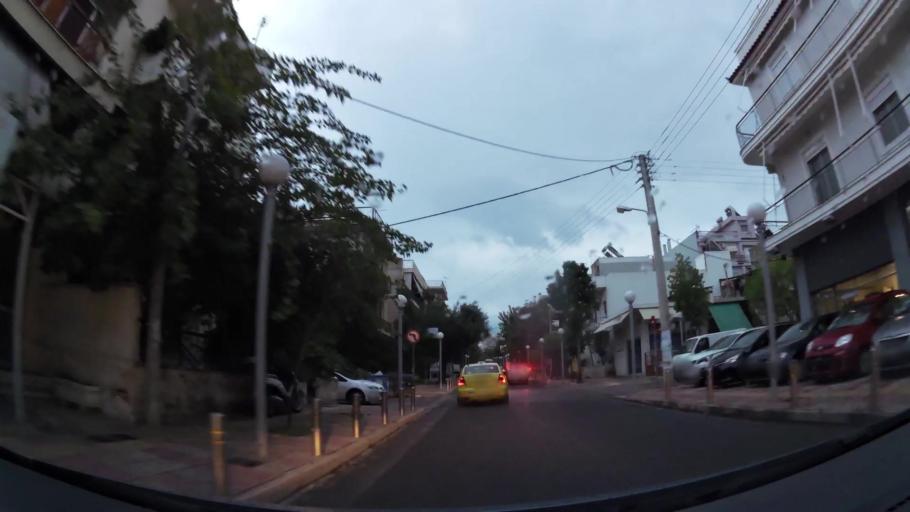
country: GR
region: Attica
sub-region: Nomarchia Athinas
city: Dhafni
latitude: 37.9489
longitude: 23.7414
